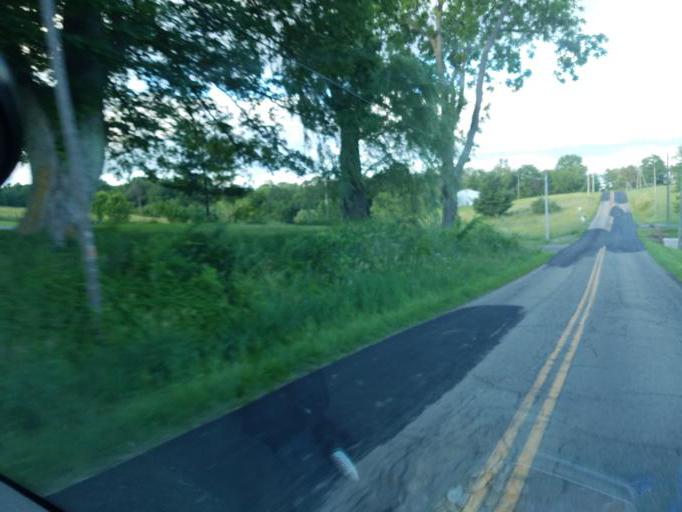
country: US
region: Ohio
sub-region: Knox County
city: Mount Vernon
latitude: 40.3825
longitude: -82.5487
